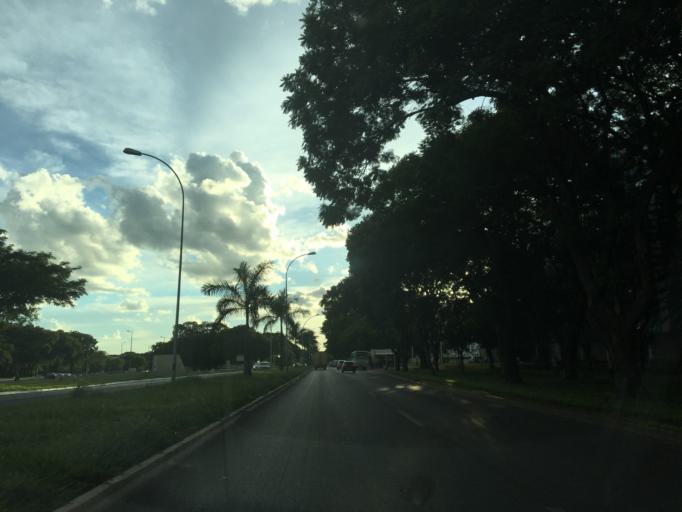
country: BR
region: Federal District
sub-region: Brasilia
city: Brasilia
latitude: -15.8255
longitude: -47.9138
